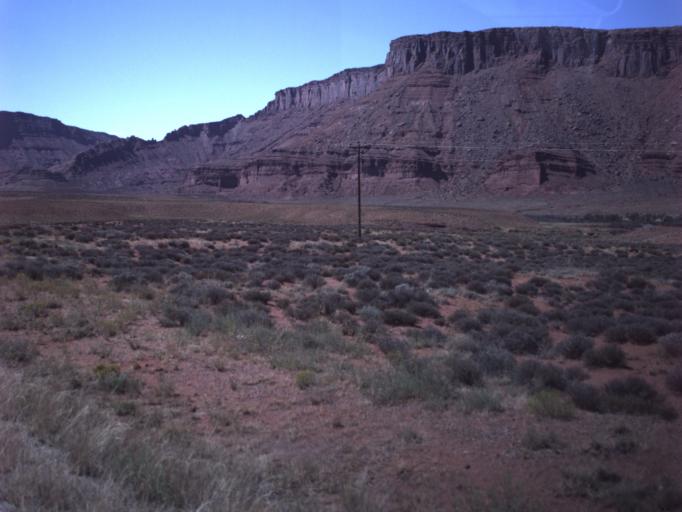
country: US
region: Utah
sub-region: Grand County
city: Moab
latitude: 38.7178
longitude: -109.3667
